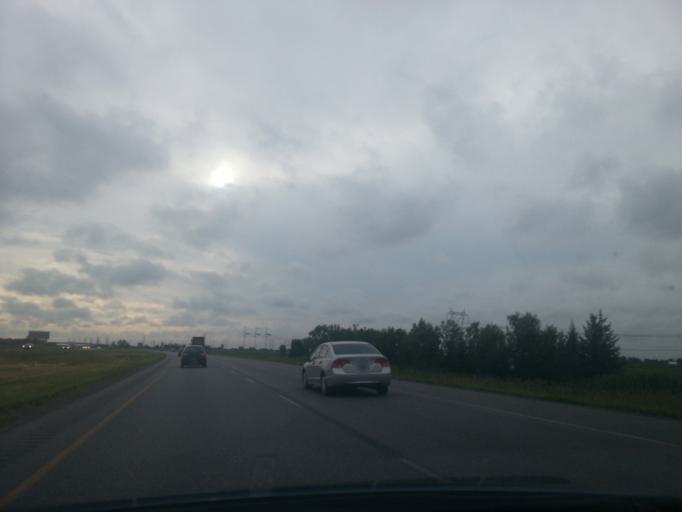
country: CA
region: Quebec
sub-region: Monteregie
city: Mercier
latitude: 45.3422
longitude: -73.6775
